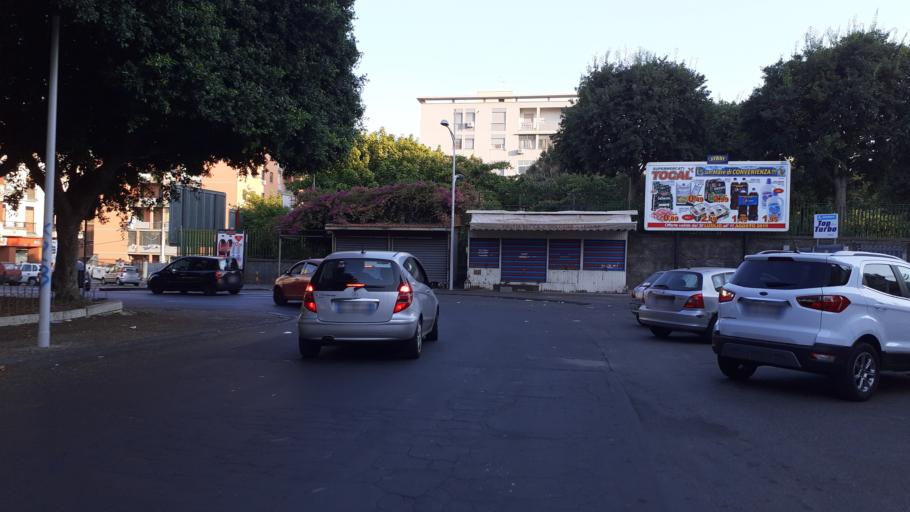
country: IT
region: Sicily
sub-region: Catania
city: Catania
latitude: 37.5011
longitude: 15.0698
